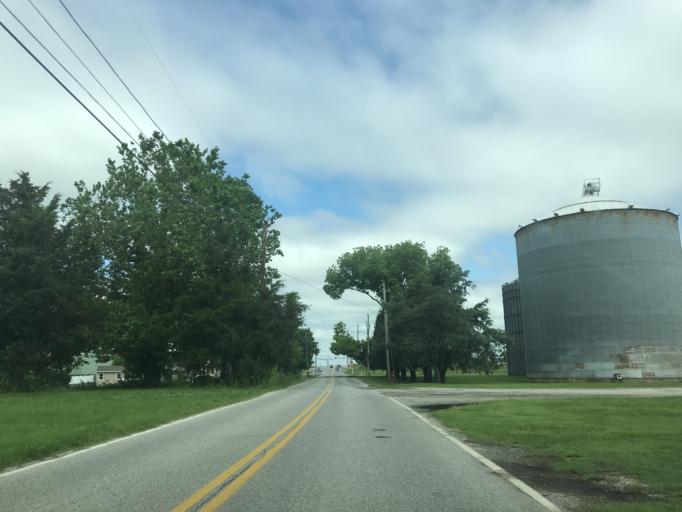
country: US
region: Maryland
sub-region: Caroline County
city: Ridgely
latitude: 38.9205
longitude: -75.9552
